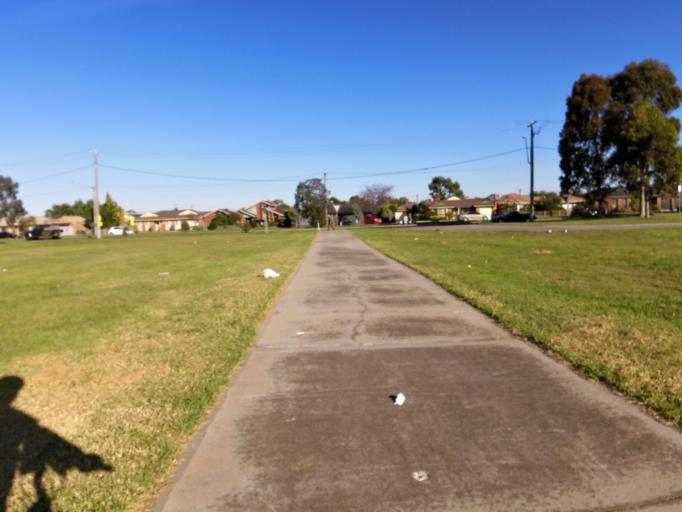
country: AU
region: Victoria
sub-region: Wyndham
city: Tarneit
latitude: -37.8626
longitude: 144.6879
